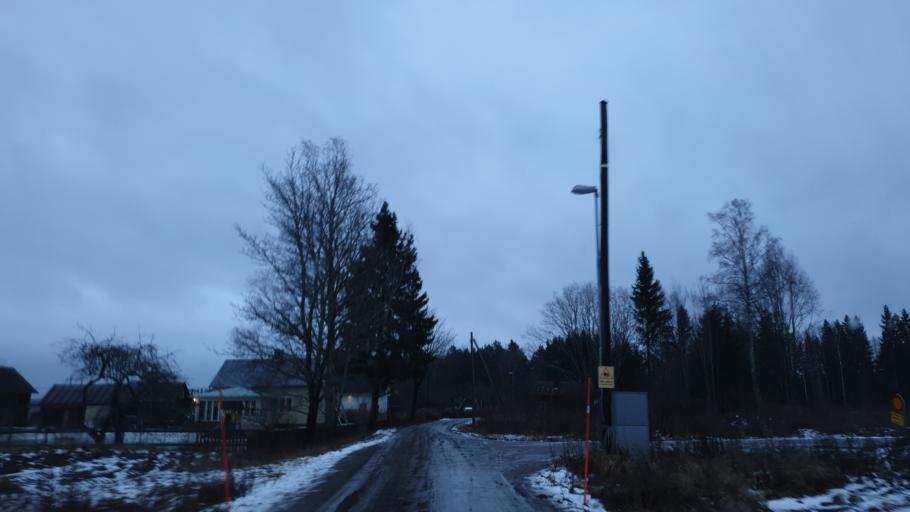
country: SE
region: Uppsala
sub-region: Tierps Kommun
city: Tierp
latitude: 60.3428
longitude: 17.4716
